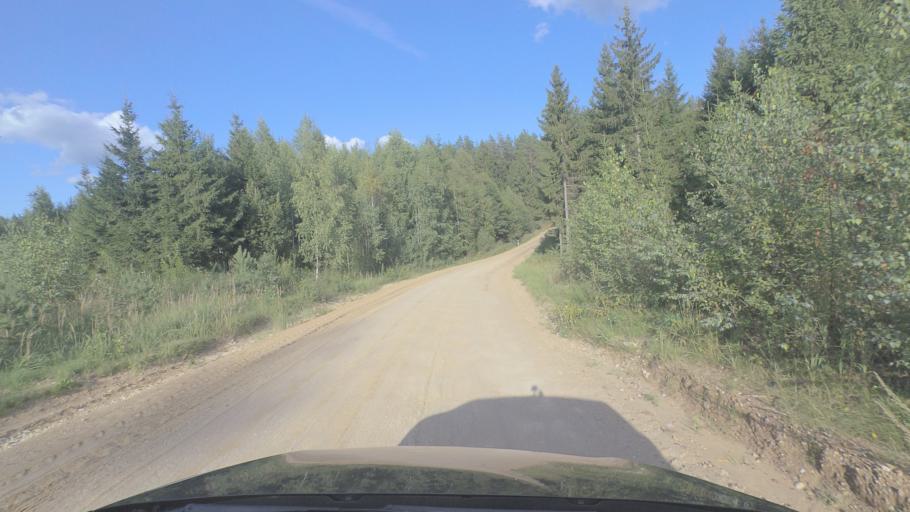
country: LT
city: Pabrade
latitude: 55.1549
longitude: 25.7891
